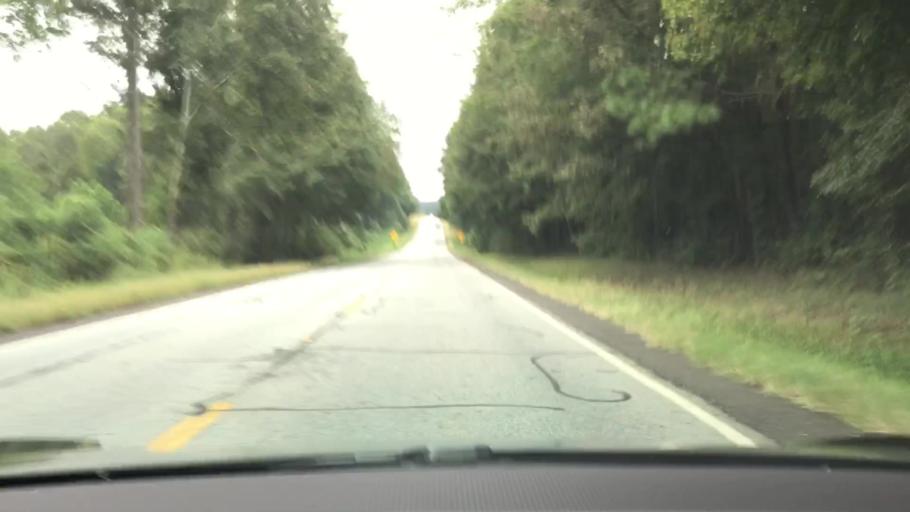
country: US
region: Georgia
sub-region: Barrow County
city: Russell
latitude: 33.9580
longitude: -83.6604
